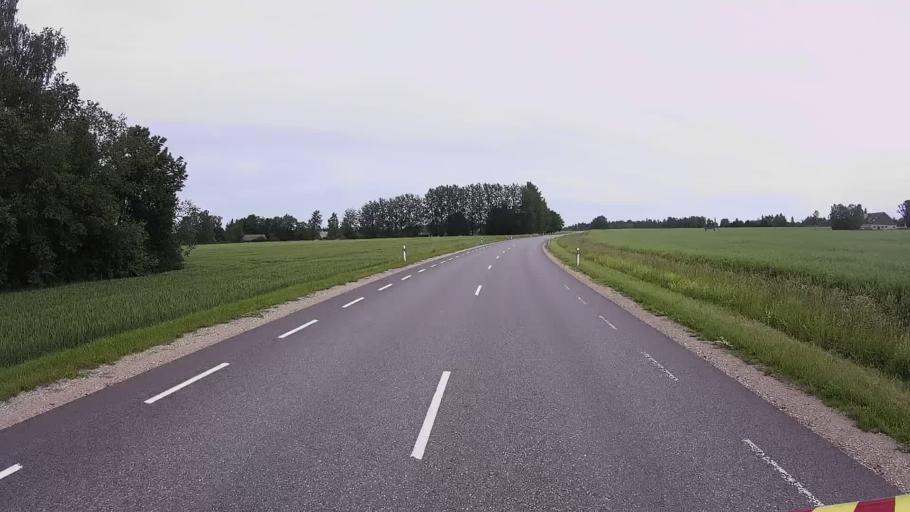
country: EE
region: Viljandimaa
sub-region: Karksi vald
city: Karksi-Nuia
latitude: 58.1736
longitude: 25.5826
